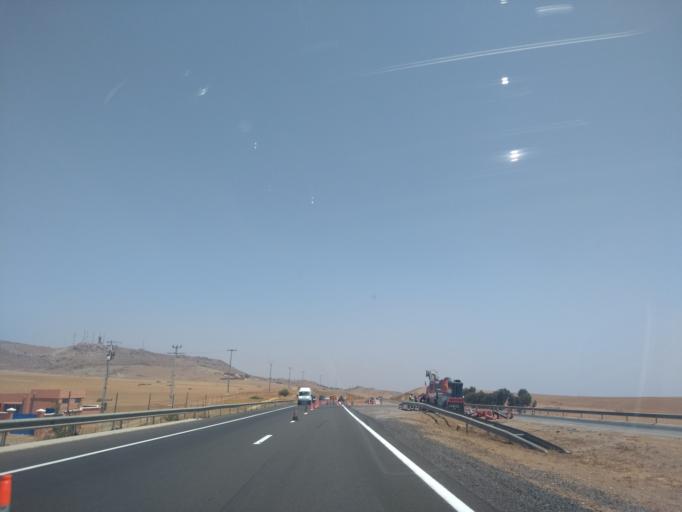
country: MA
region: Marrakech-Tensift-Al Haouz
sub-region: Kelaa-Des-Sraghna
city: Sidi Abdallah
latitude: 32.4549
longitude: -7.9312
